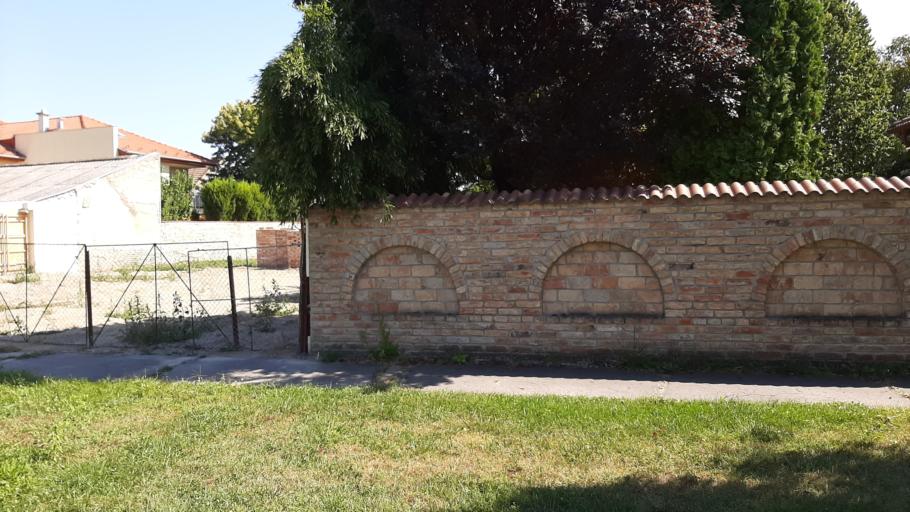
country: HU
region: Csongrad
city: Szeged
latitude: 46.2386
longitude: 20.1275
